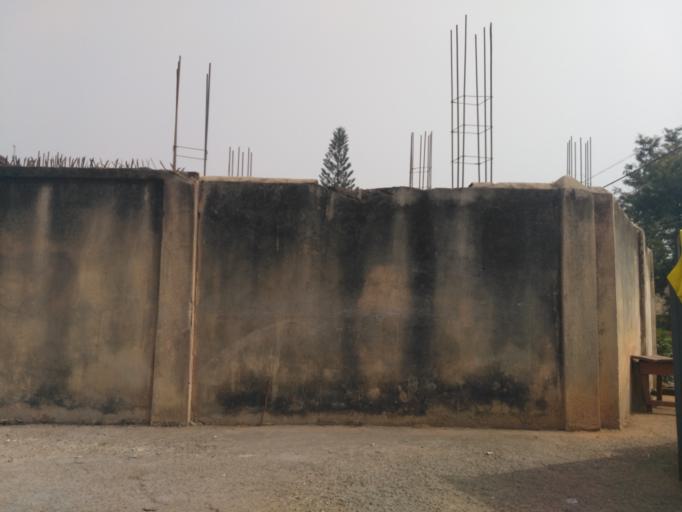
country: GH
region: Ashanti
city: Kumasi
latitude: 6.6735
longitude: -1.6051
